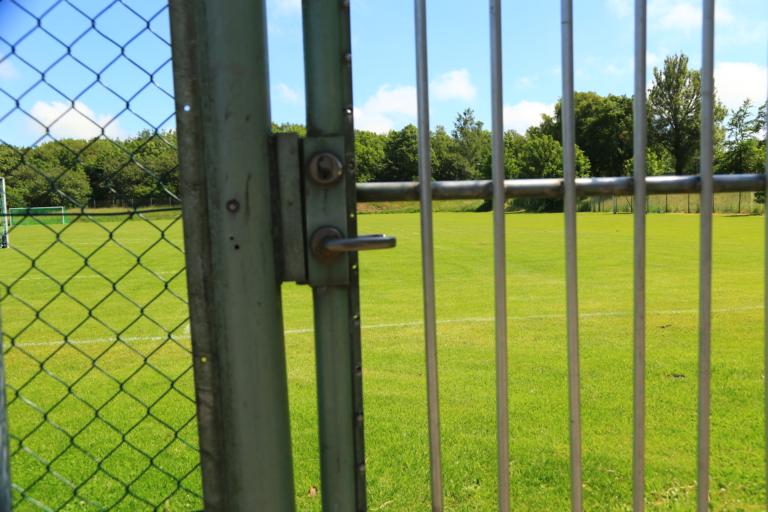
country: SE
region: Halland
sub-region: Varbergs Kommun
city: Varberg
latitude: 57.1045
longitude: 12.2820
